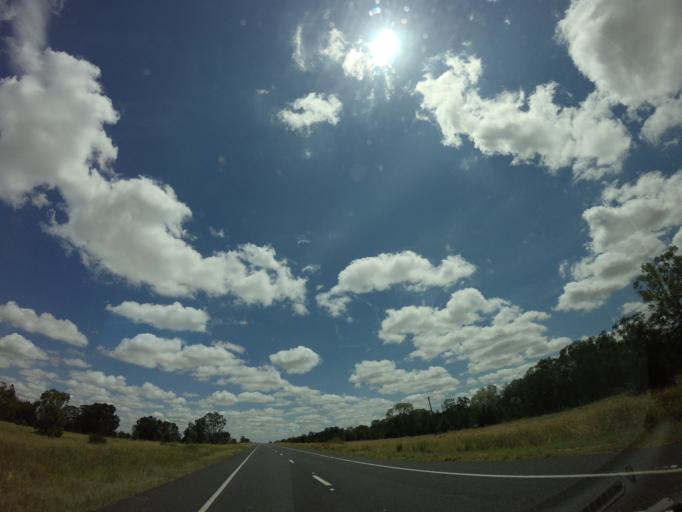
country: AU
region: New South Wales
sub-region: Moree Plains
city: Moree
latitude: -29.1318
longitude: 150.0240
